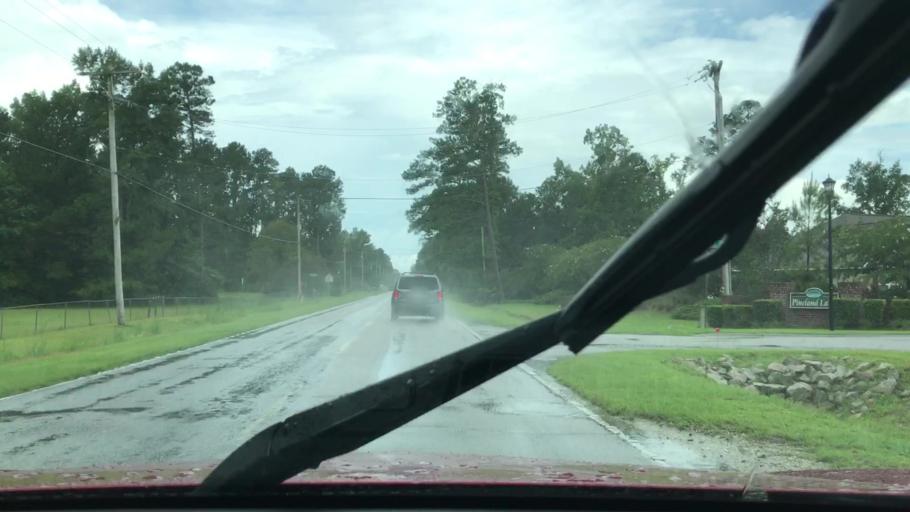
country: US
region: South Carolina
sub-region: Horry County
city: Red Hill
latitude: 33.8567
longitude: -79.0040
